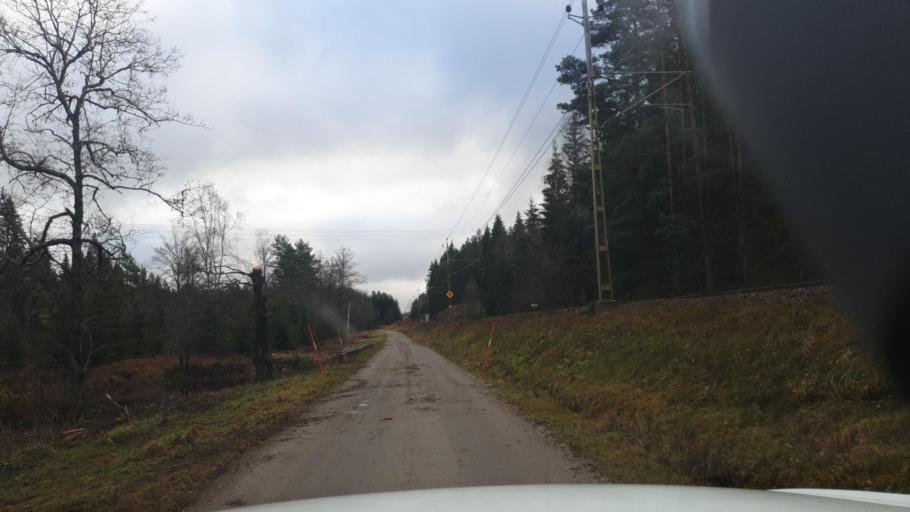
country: SE
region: Vaermland
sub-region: Karlstads Kommun
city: Edsvalla
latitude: 59.6137
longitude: 12.9753
